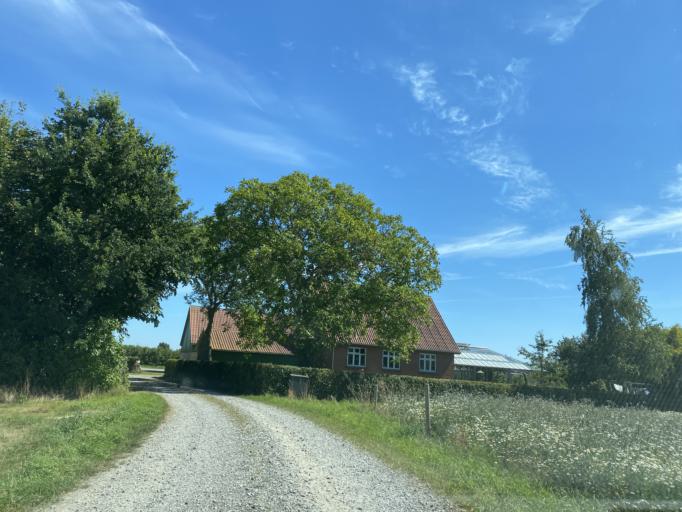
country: DK
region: South Denmark
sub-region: Nyborg Kommune
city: Ullerslev
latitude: 55.3807
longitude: 10.7288
